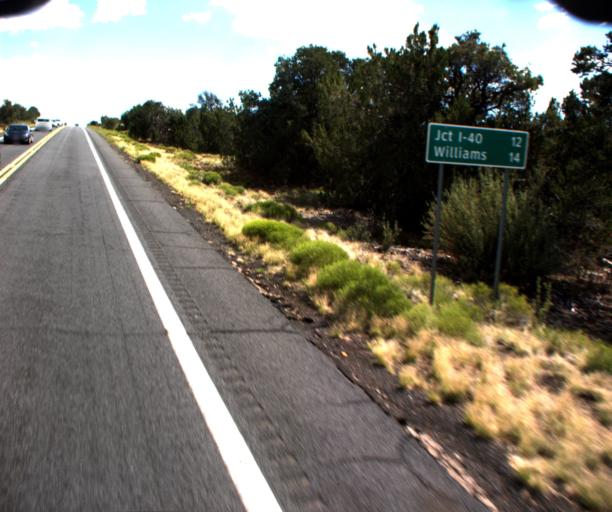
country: US
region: Arizona
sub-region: Coconino County
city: Williams
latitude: 35.4200
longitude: -112.1705
